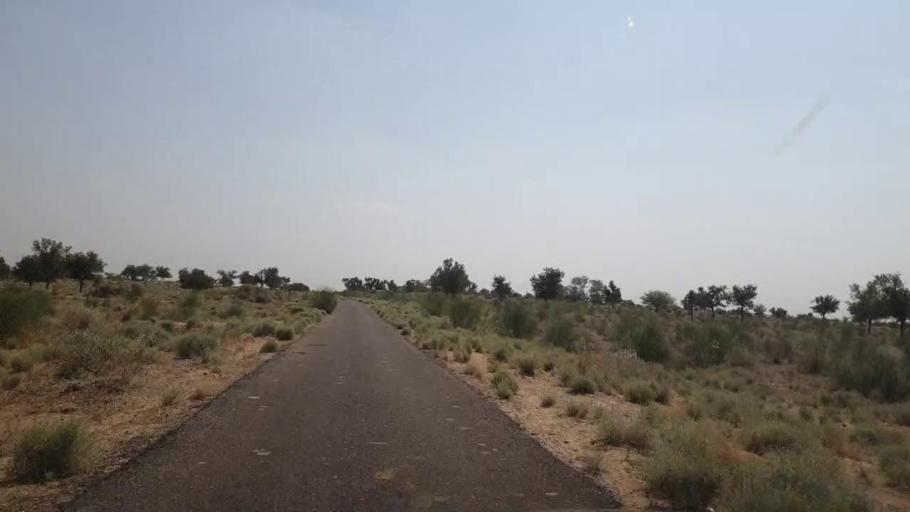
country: PK
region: Sindh
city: Islamkot
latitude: 25.0972
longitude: 70.7282
